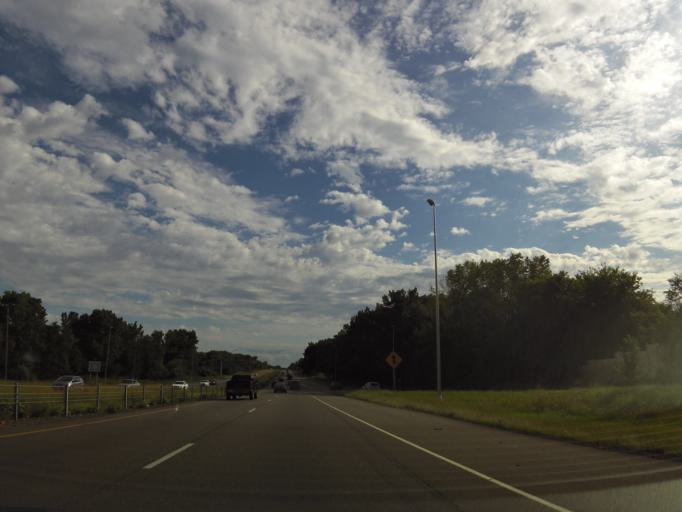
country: US
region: Minnesota
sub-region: Hennepin County
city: Osseo
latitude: 45.0809
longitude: -93.4023
